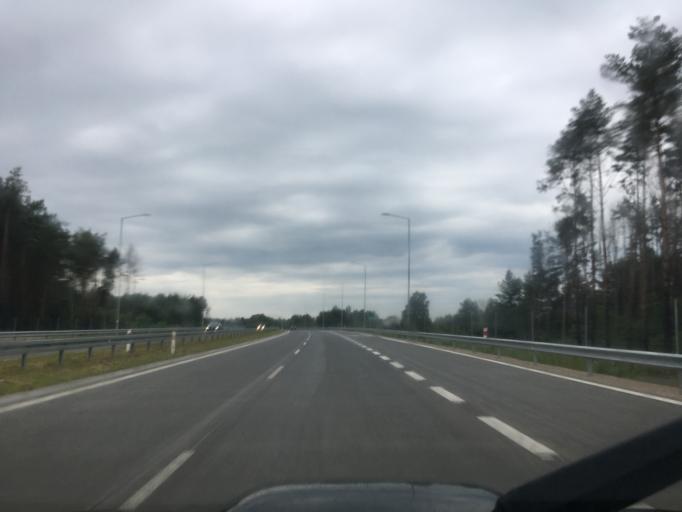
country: PL
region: Masovian Voivodeship
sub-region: Powiat piaseczynski
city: Gora Kalwaria
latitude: 51.9749
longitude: 21.1902
